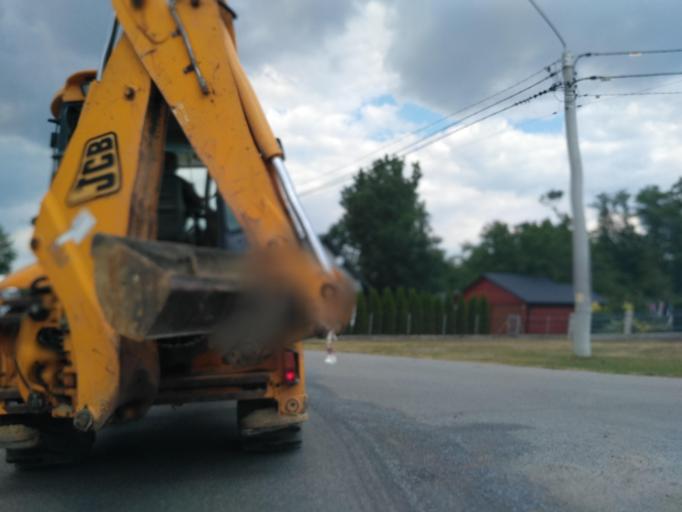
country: PL
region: Subcarpathian Voivodeship
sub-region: Powiat debicki
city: Zyrakow
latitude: 50.0486
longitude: 21.3420
